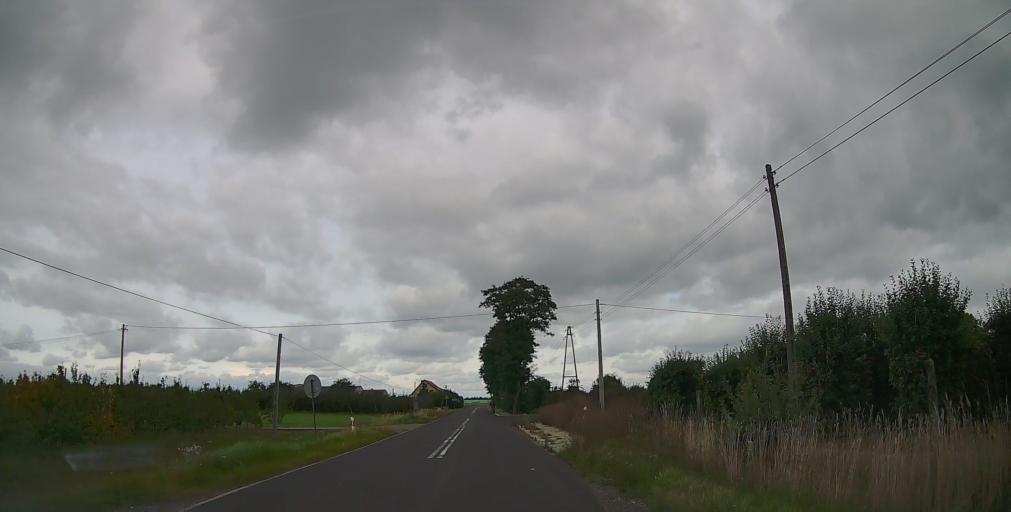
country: PL
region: Masovian Voivodeship
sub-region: Powiat grojecki
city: Goszczyn
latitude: 51.7635
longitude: 20.8976
